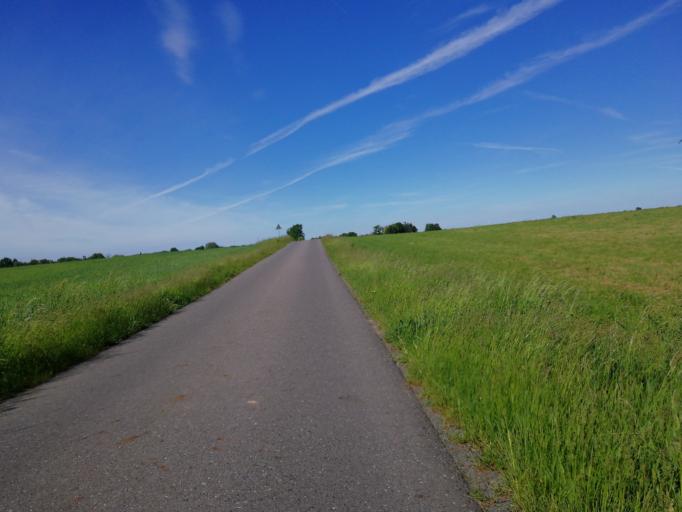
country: DE
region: Brandenburg
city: Calau
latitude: 51.7375
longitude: 13.9177
